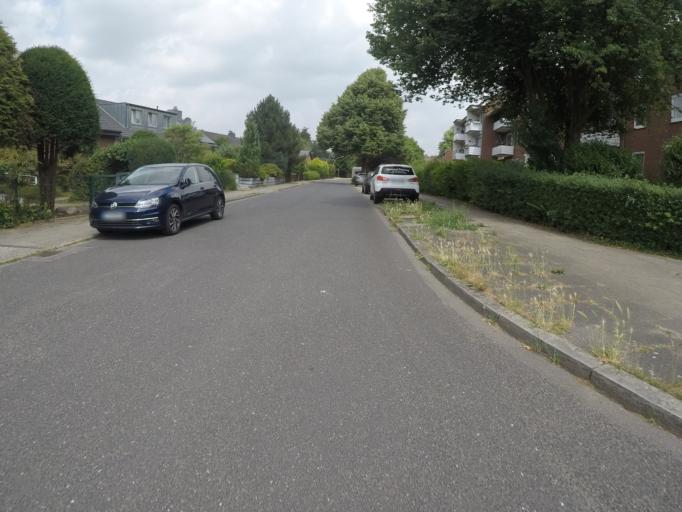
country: DE
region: Schleswig-Holstein
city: Bonningstedt
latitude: 53.6356
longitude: 9.9387
